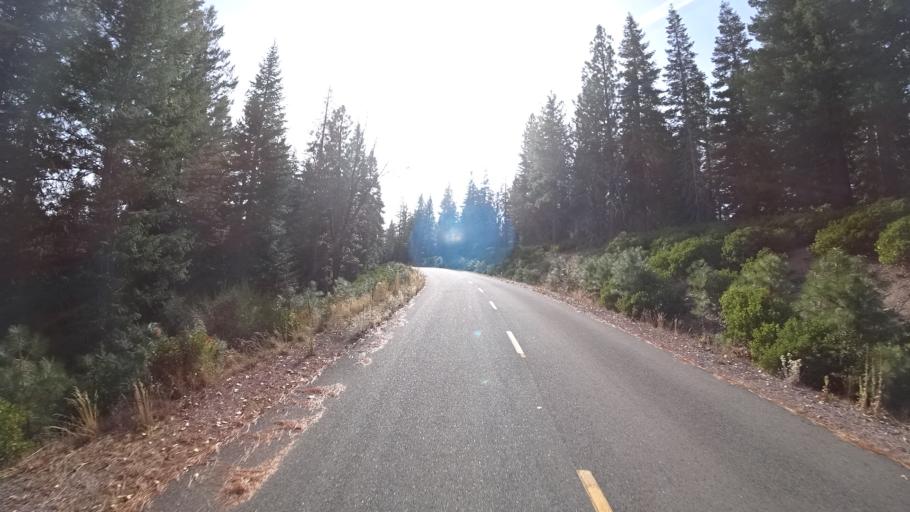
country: US
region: California
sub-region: Siskiyou County
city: Weed
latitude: 41.3956
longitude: -122.3926
